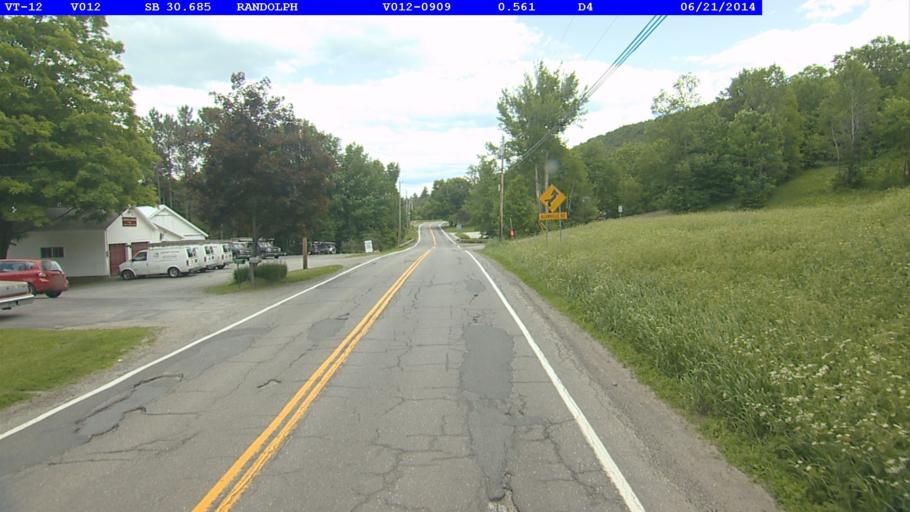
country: US
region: Vermont
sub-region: Orange County
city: Randolph
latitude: 43.9023
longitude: -72.6572
